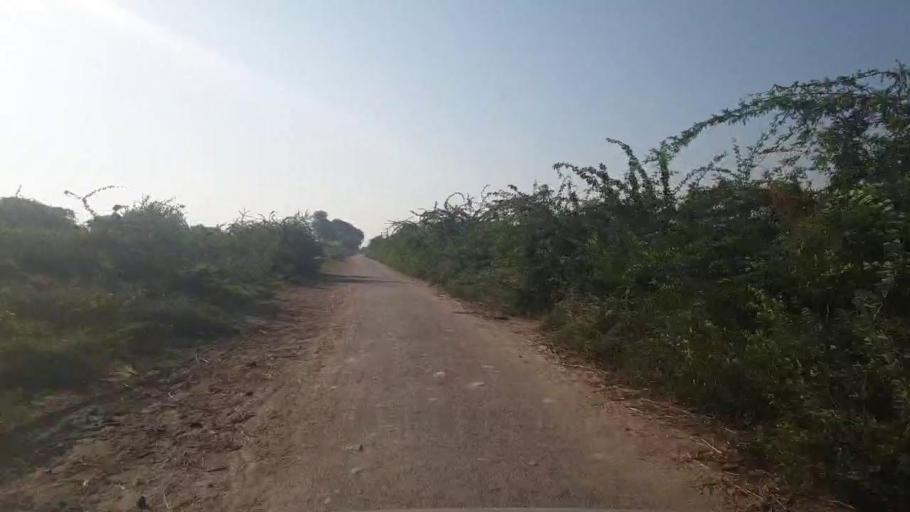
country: PK
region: Sindh
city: Tando Bago
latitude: 24.7382
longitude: 68.9304
